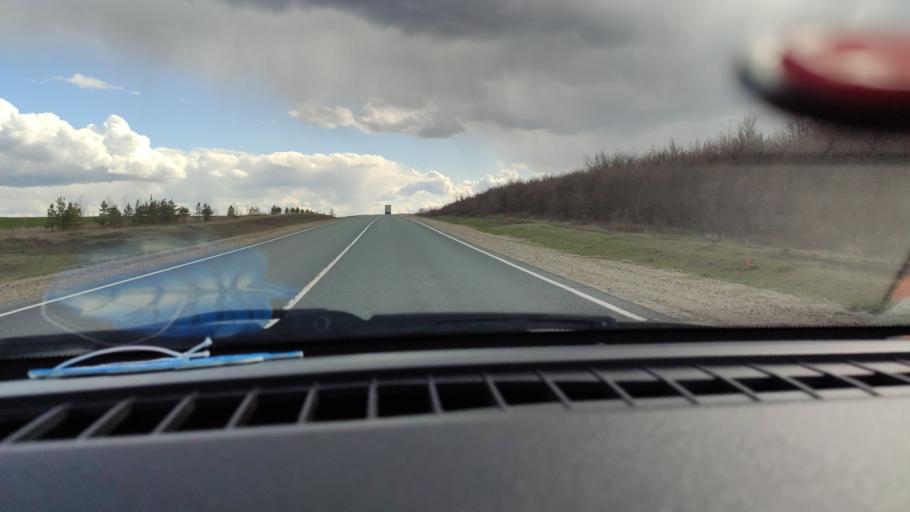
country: RU
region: Saratov
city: Alekseyevka
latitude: 52.2343
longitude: 47.9041
